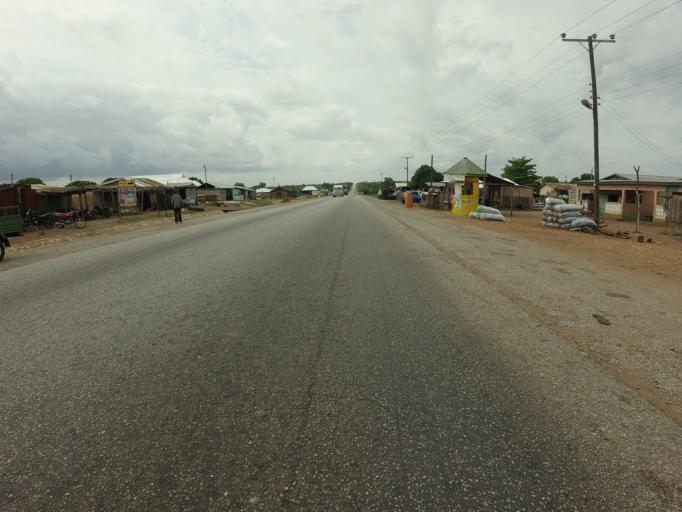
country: GH
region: Brong-Ahafo
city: Kintampo
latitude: 8.6634
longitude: -1.5198
